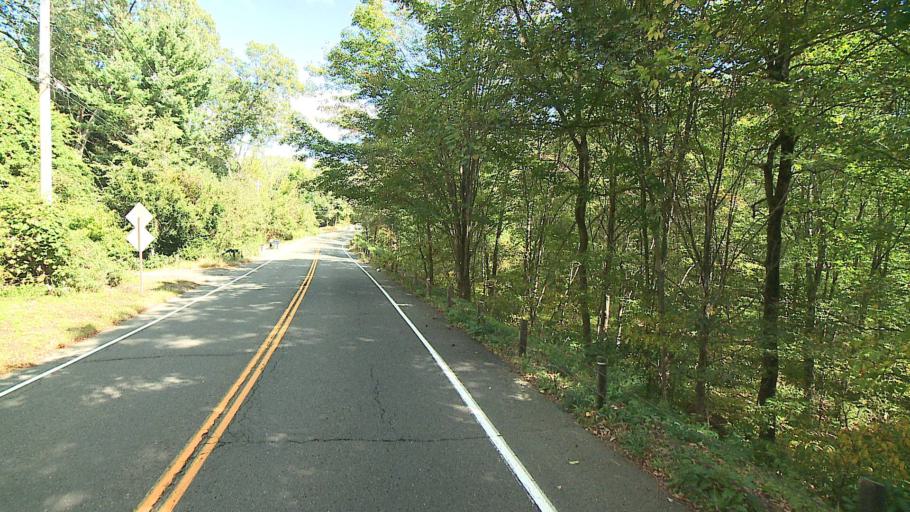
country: US
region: Connecticut
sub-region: New Haven County
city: Oxford
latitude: 41.4307
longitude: -73.1041
